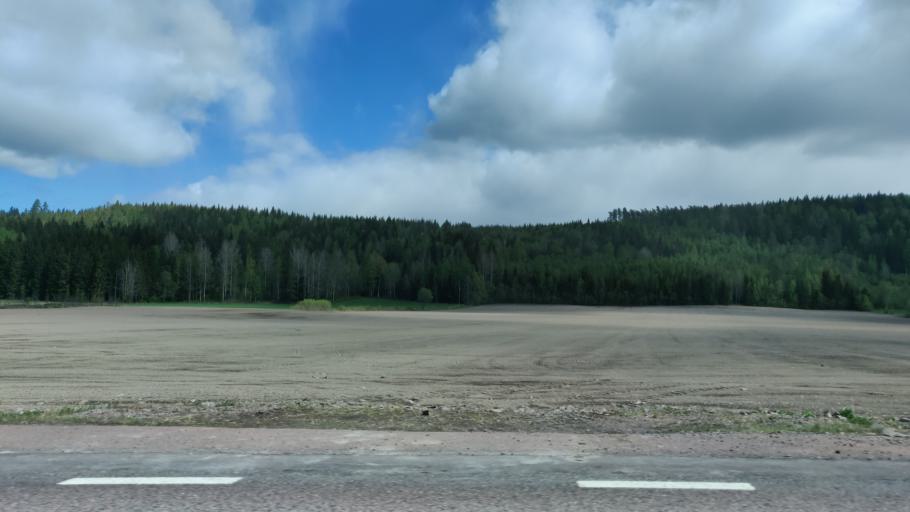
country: SE
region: Vaermland
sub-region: Karlstads Kommun
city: Molkom
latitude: 59.6317
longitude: 13.7257
